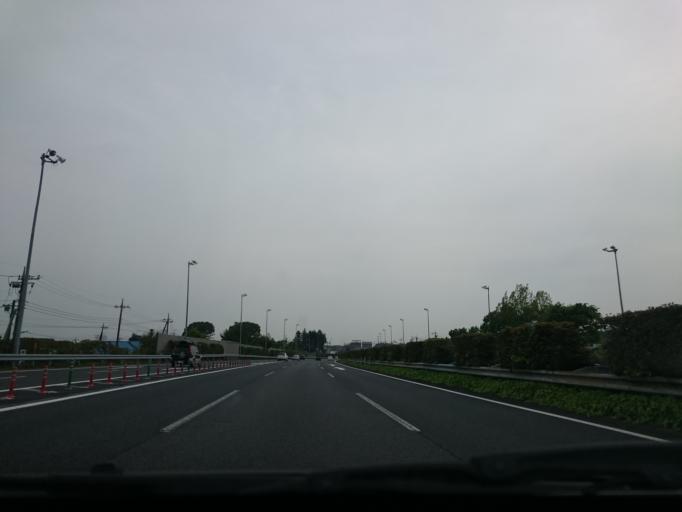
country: JP
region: Tochigi
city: Kanuma
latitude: 36.5382
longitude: 139.7988
